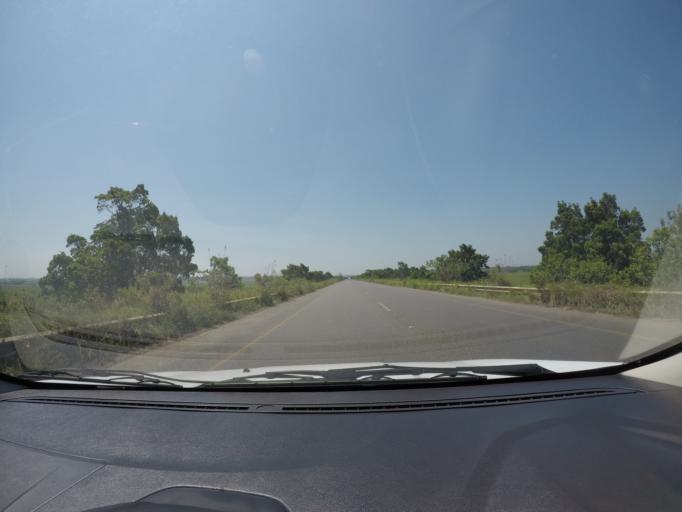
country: ZA
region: KwaZulu-Natal
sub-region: uThungulu District Municipality
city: Empangeni
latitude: -28.7899
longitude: 31.9581
